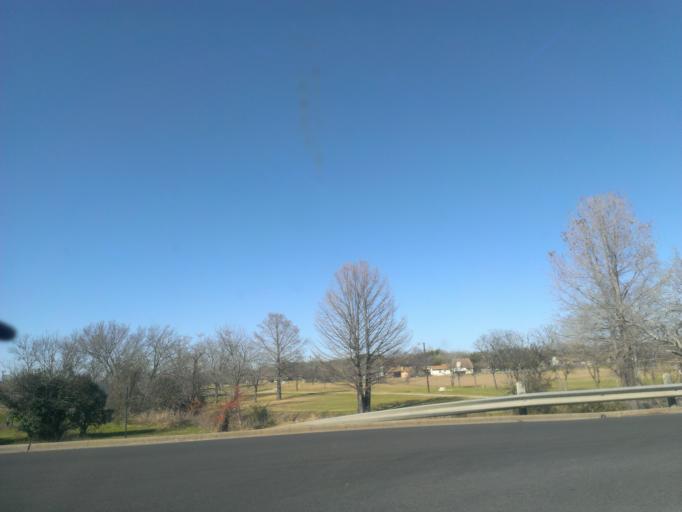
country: US
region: Texas
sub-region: Williamson County
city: Taylor
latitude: 30.5818
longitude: -97.4156
